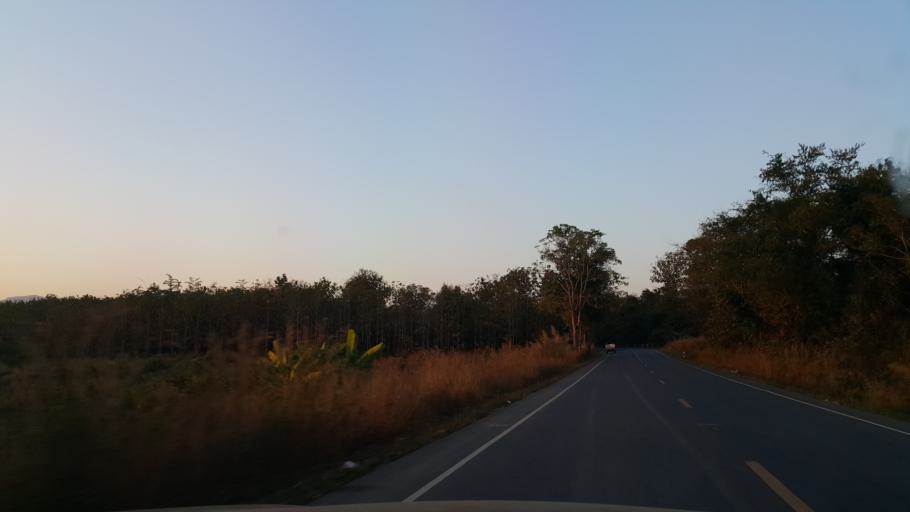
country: TH
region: Phrae
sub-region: Amphoe Wang Chin
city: Wang Chin
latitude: 17.8573
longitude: 99.6266
